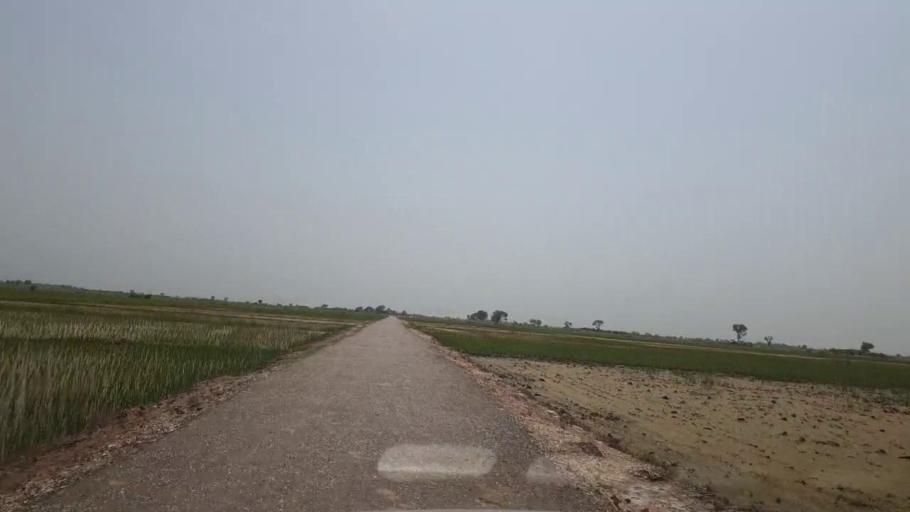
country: PK
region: Sindh
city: Garhi Yasin
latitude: 28.0629
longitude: 68.3189
